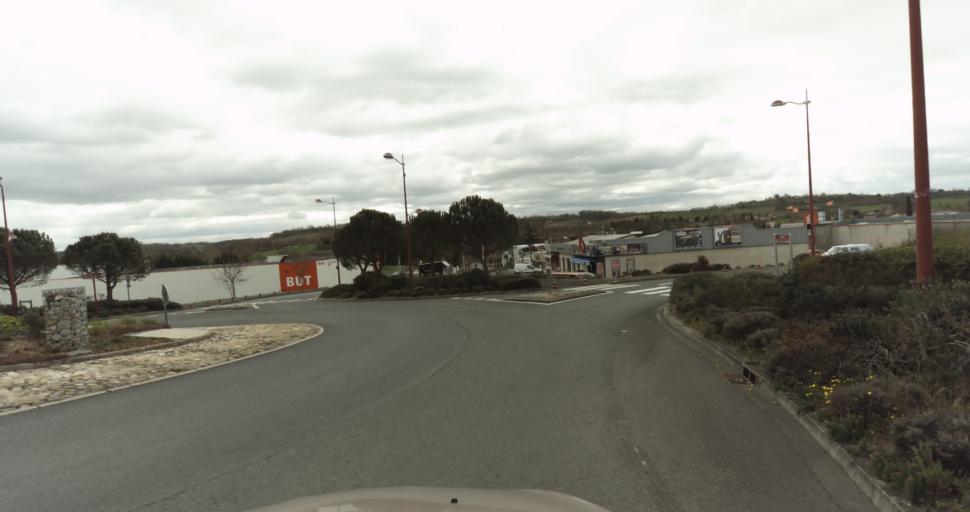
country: FR
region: Midi-Pyrenees
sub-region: Departement du Tarn
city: Puygouzon
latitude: 43.8924
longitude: 2.1655
